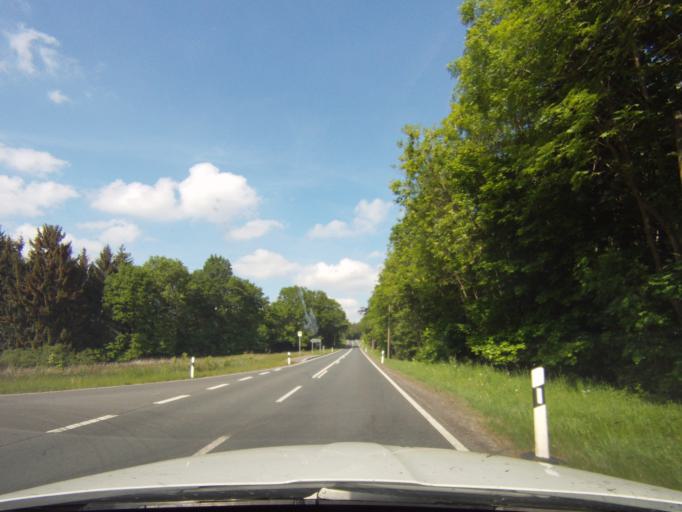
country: DE
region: Thuringia
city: Hundhaupten
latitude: 50.8182
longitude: 11.9882
